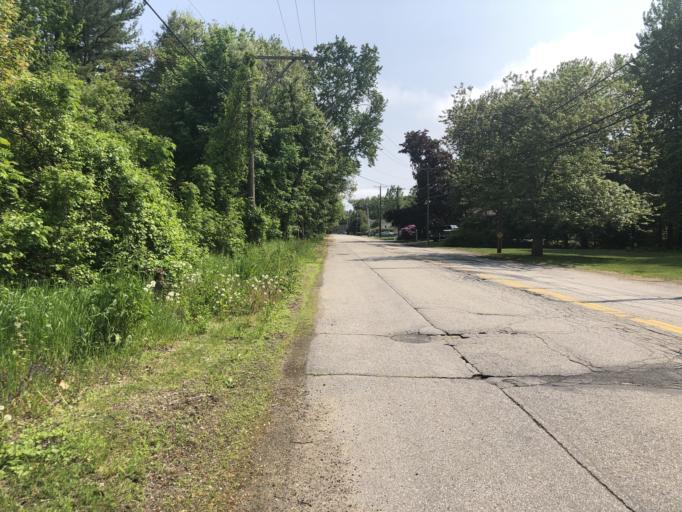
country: US
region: Maine
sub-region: York County
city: Eliot
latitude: 43.1306
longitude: -70.8361
